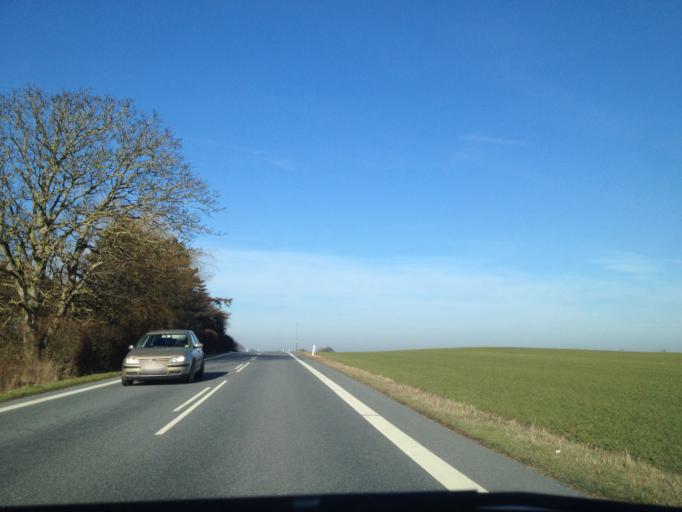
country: DK
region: South Denmark
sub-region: Kerteminde Kommune
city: Kerteminde
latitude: 55.4852
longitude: 10.6593
